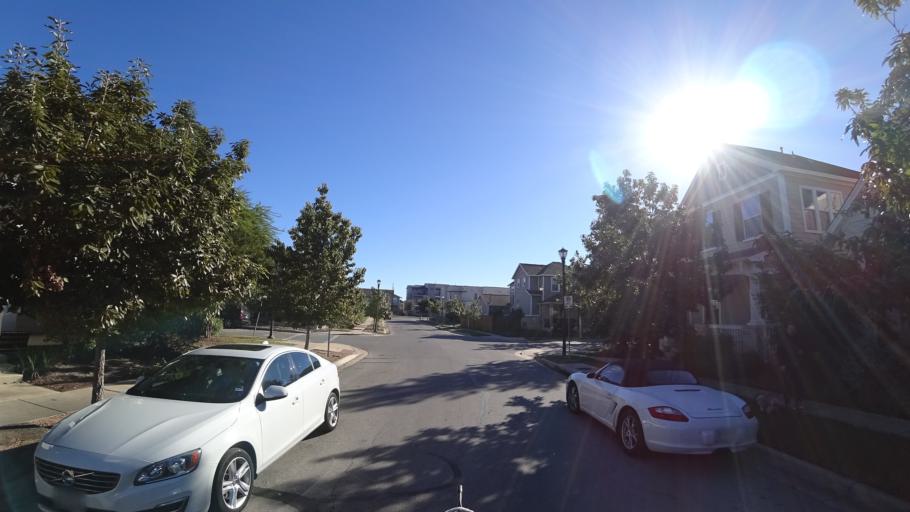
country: US
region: Texas
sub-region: Travis County
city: Austin
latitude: 30.2929
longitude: -97.7011
